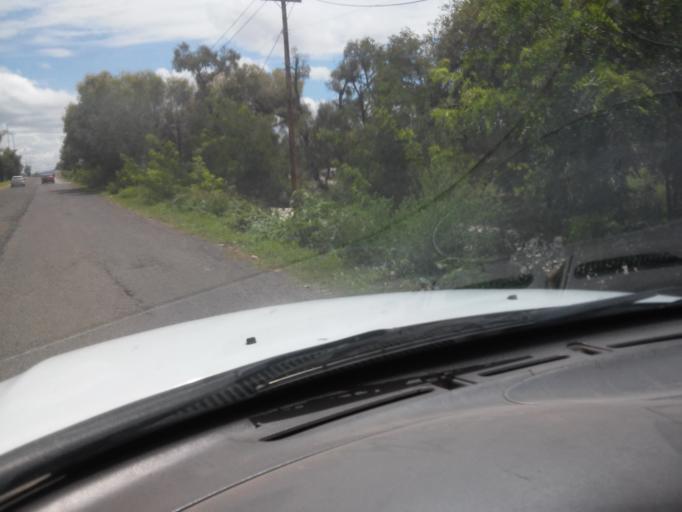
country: MX
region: Durango
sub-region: Durango
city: Jose Refugio Salcido
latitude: 24.0254
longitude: -104.5663
